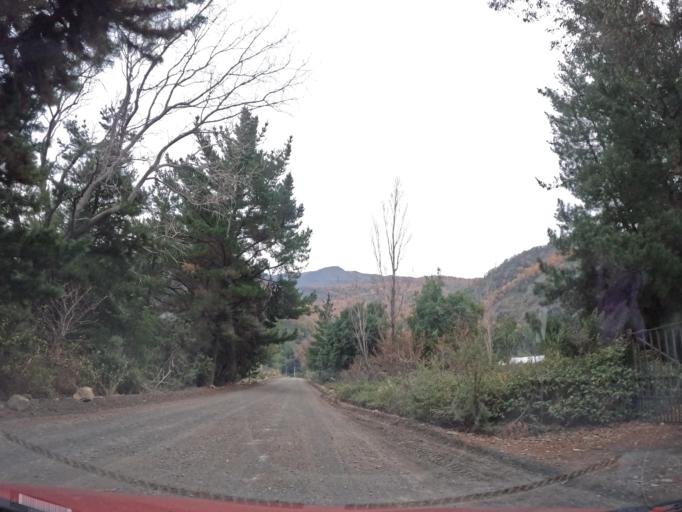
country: CL
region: Maule
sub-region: Provincia de Linares
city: Colbun
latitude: -35.7032
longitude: -71.0985
